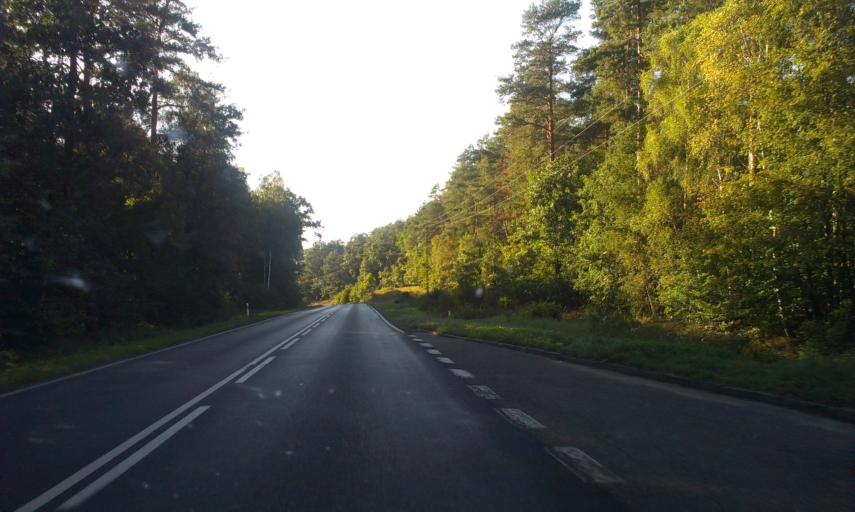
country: PL
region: Kujawsko-Pomorskie
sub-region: Powiat tucholski
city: Tuchola
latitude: 53.5540
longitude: 17.9104
